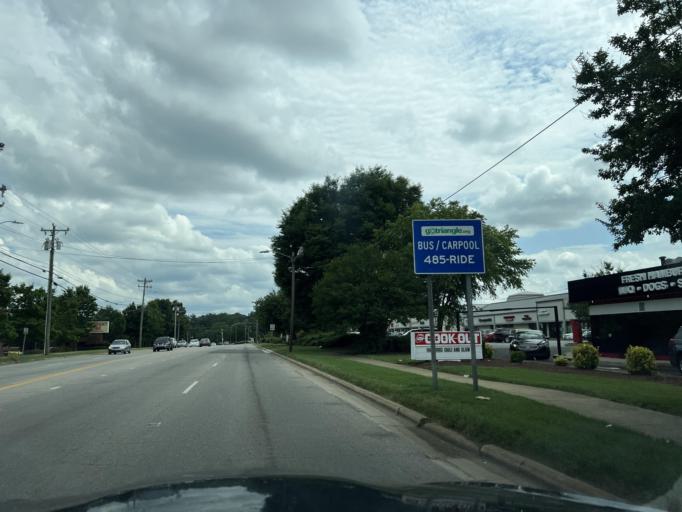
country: US
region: North Carolina
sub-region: Durham County
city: Durham
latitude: 36.0503
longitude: -78.9036
